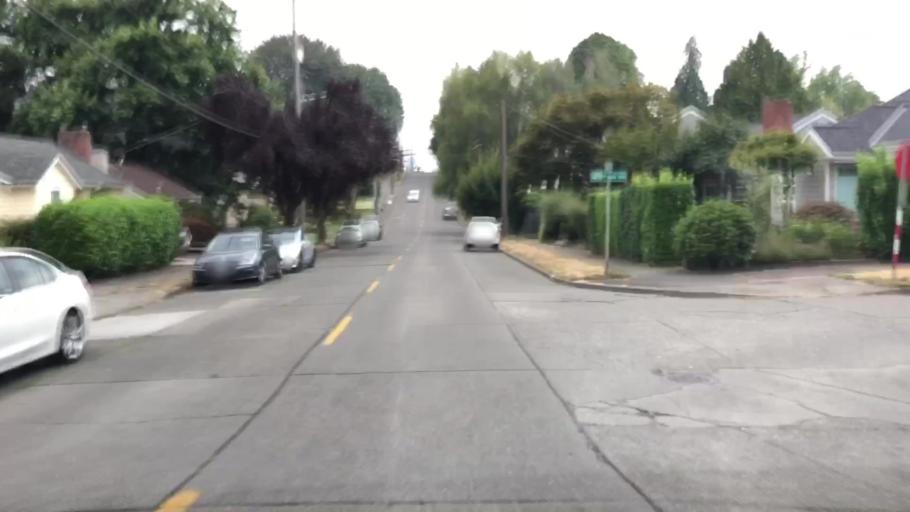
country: US
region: Washington
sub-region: King County
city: Yarrow Point
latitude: 47.6613
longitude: -122.2743
